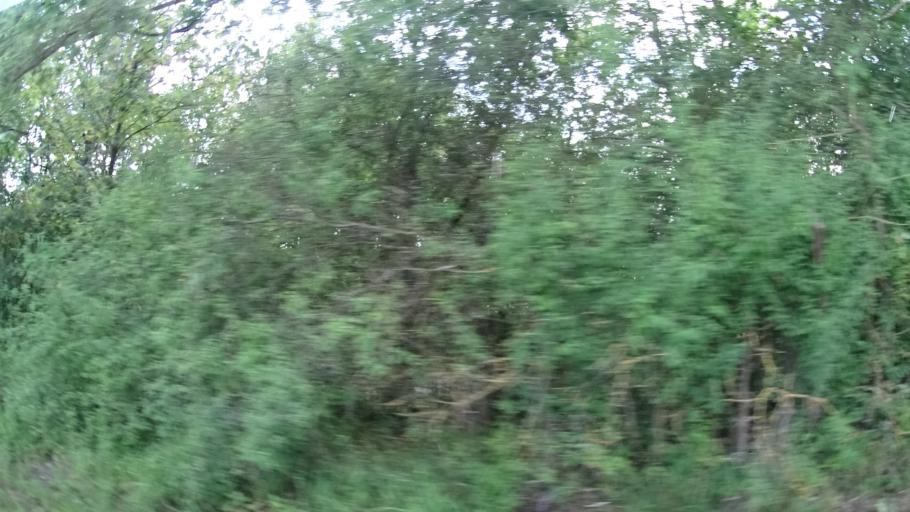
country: DE
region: Thuringia
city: Hildburghausen
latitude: 50.3805
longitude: 10.7457
